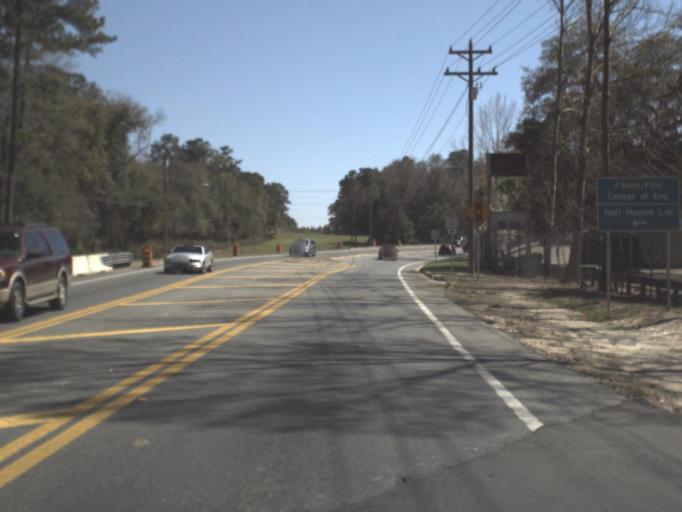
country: US
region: Florida
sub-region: Leon County
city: Tallahassee
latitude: 30.4215
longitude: -84.3516
